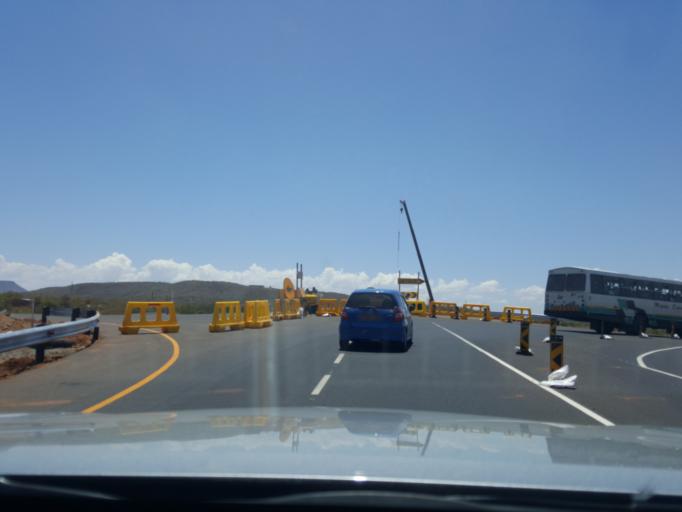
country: BW
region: South East
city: Ramotswa
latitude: -24.8284
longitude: 25.8074
